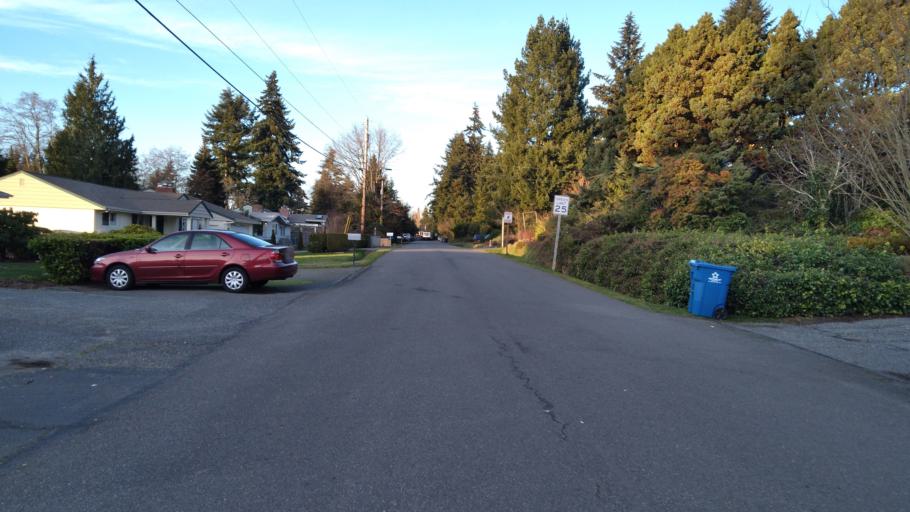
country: US
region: Washington
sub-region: Snohomish County
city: Esperance
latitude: 47.7929
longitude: -122.3540
